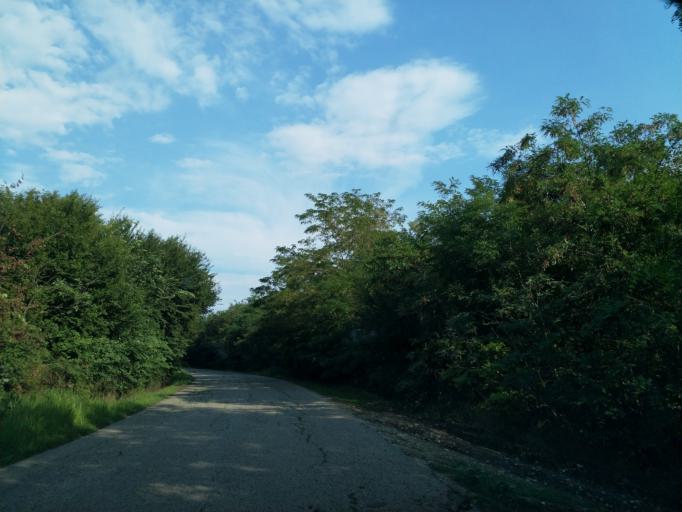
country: RS
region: Central Serbia
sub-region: Pomoravski Okrug
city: Jagodina
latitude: 43.9937
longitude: 21.1987
